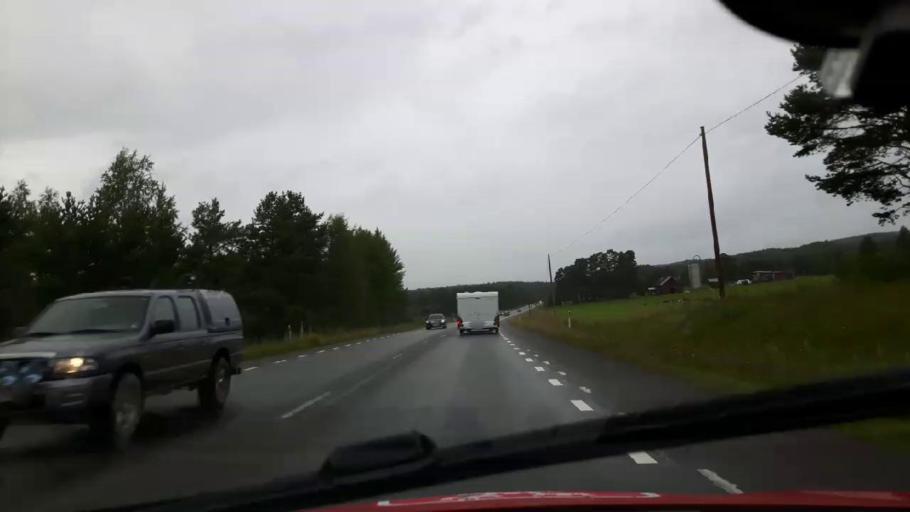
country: SE
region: Jaemtland
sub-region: Are Kommun
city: Jarpen
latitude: 63.3293
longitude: 13.5294
